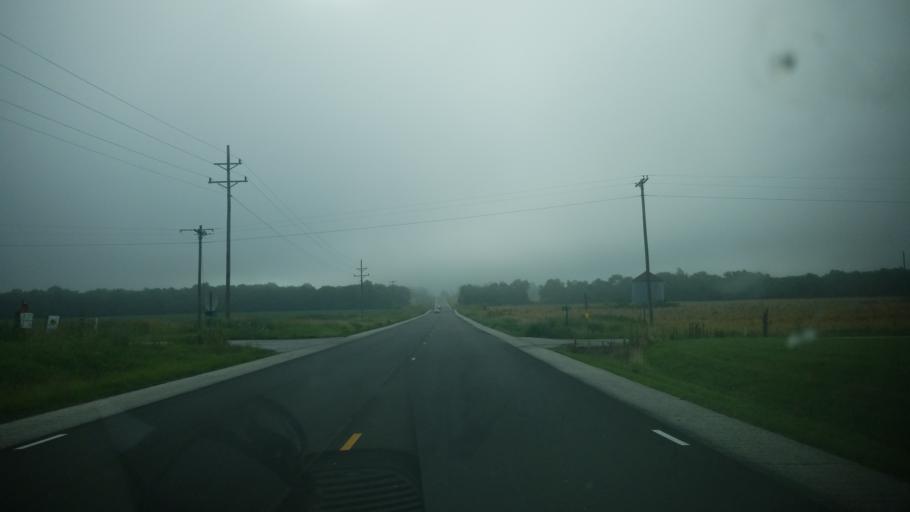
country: US
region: Missouri
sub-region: Pike County
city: Bowling Green
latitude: 39.3444
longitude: -91.2800
